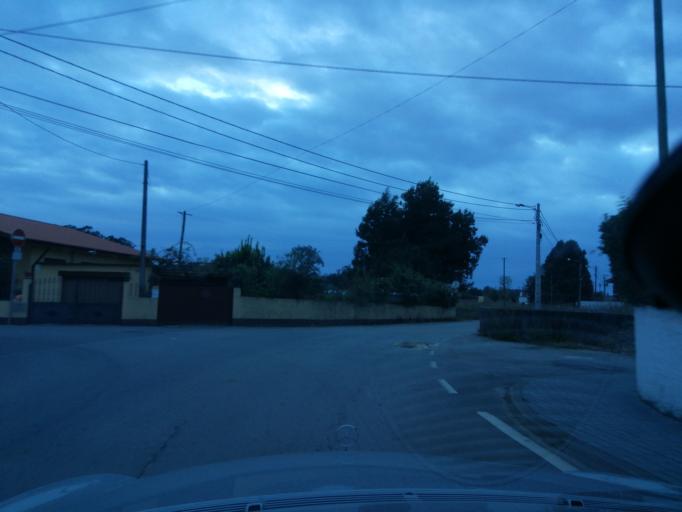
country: PT
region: Aveiro
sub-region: Estarreja
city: Estarreja
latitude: 40.7646
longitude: -8.5880
